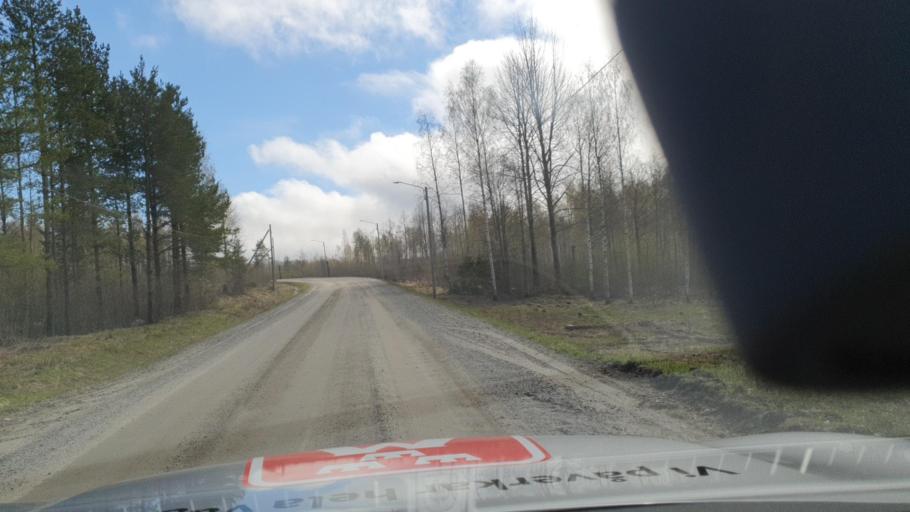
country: SE
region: Vaesterbotten
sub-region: Bjurholms Kommun
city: Bjurholm
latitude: 63.6895
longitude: 18.9578
